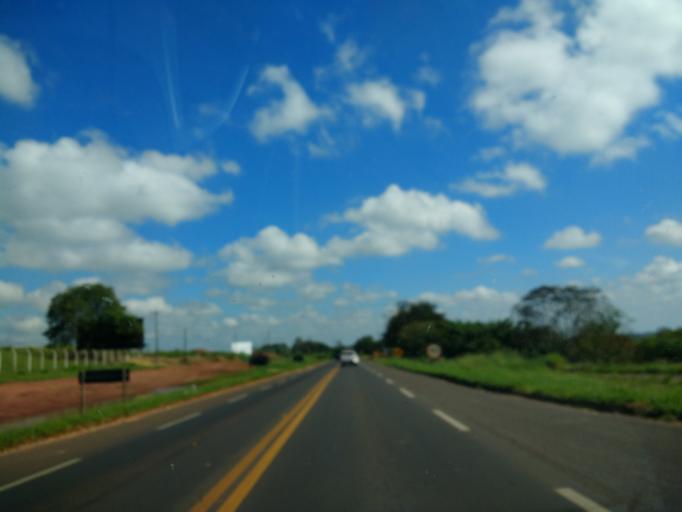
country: BR
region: Parana
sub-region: Umuarama
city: Umuarama
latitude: -23.8132
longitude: -53.3273
